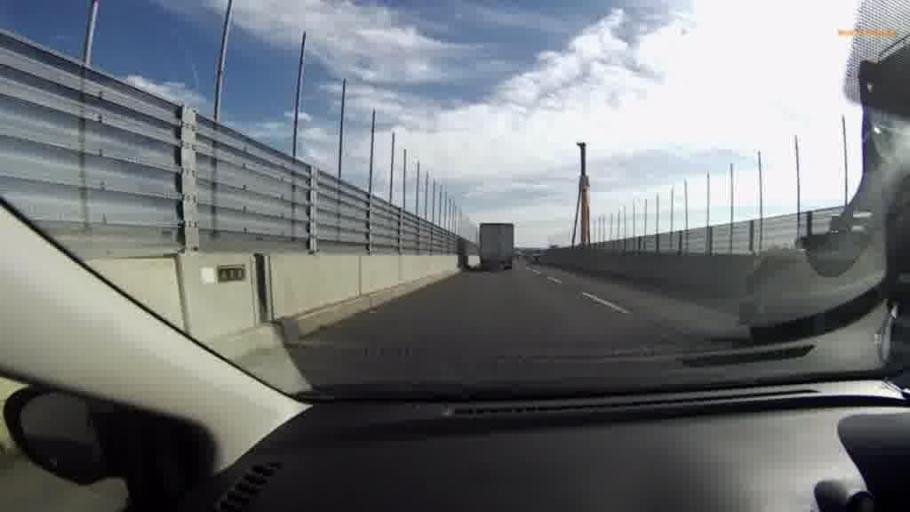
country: JP
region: Hokkaido
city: Kushiro
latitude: 43.0364
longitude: 144.3232
